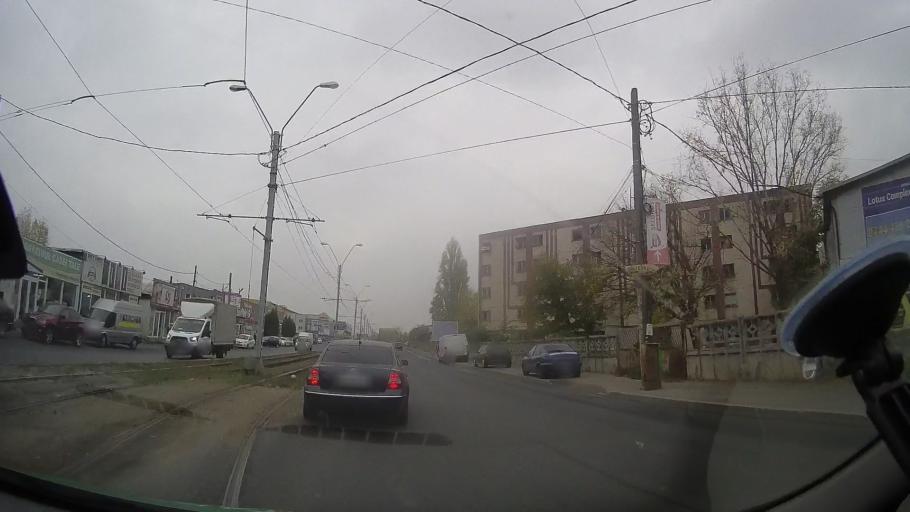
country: RO
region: Ilfov
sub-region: Comuna Chiajna
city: Rosu
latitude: 44.4287
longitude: 26.0019
